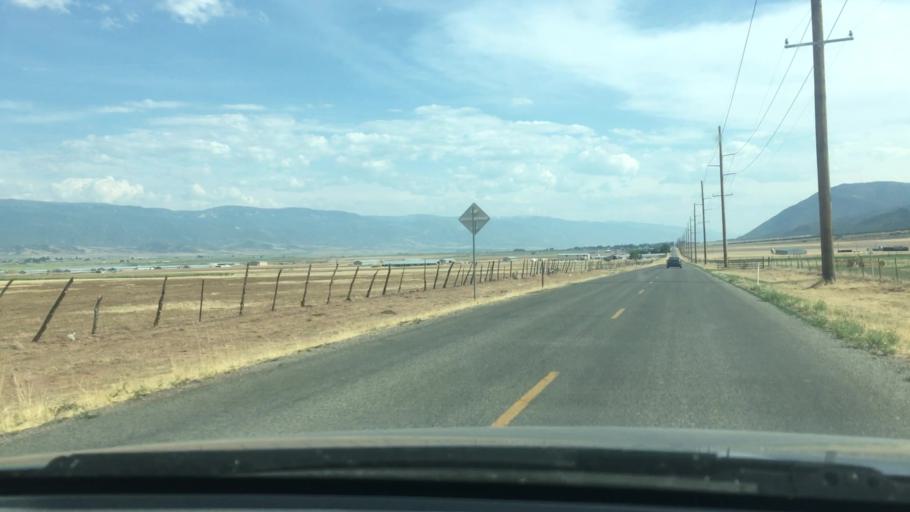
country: US
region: Utah
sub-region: Sanpete County
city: Moroni
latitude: 39.5384
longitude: -111.6399
